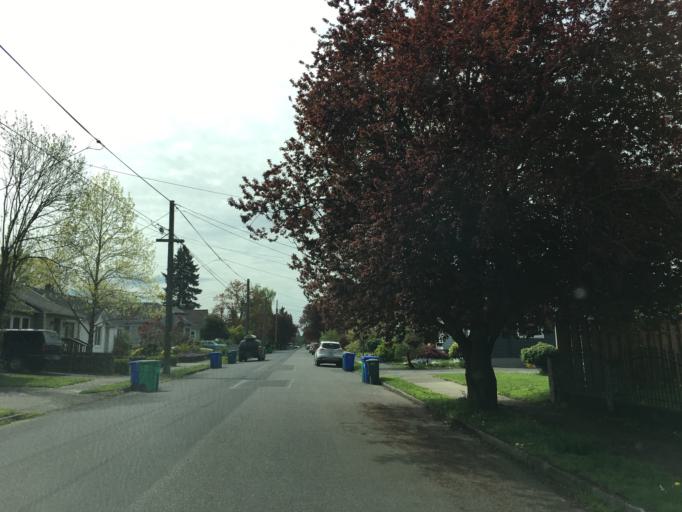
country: US
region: Oregon
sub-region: Multnomah County
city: Lents
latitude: 45.5316
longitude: -122.5858
